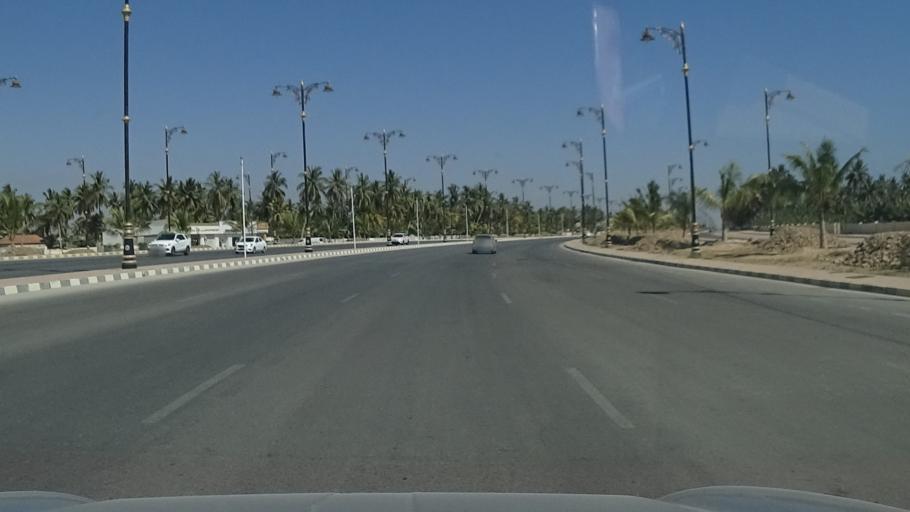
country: OM
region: Zufar
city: Salalah
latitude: 17.0362
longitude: 54.1486
